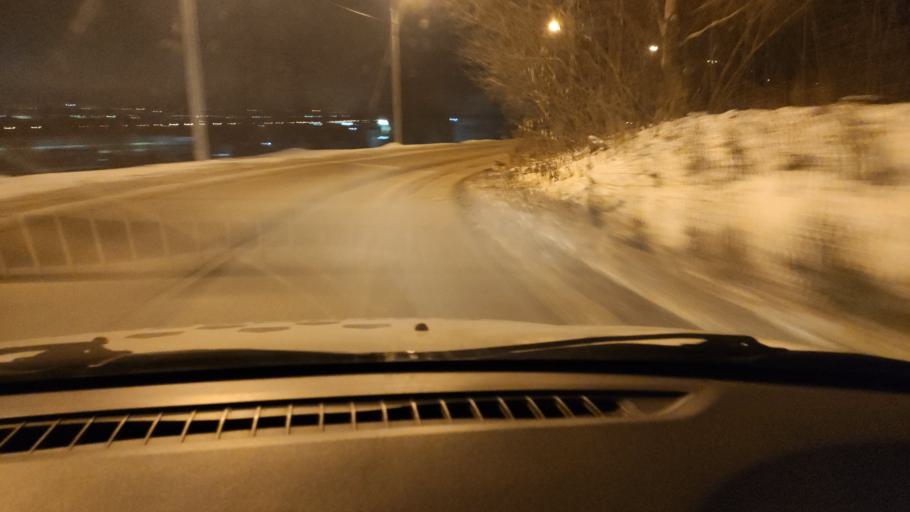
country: RU
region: Perm
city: Perm
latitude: 58.1035
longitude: 56.3097
